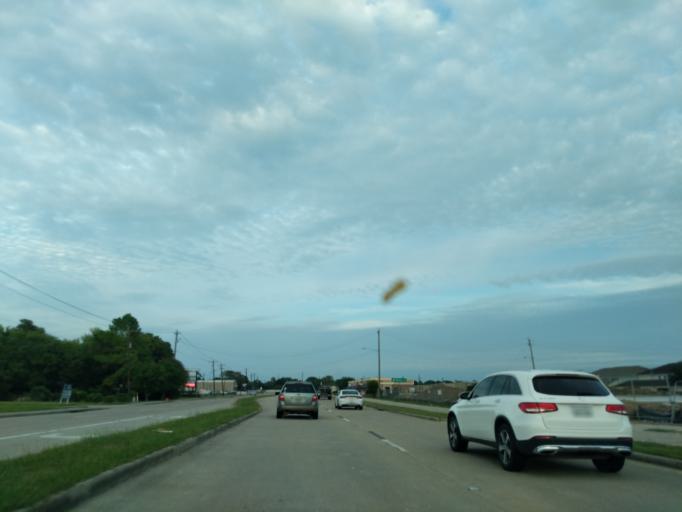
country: US
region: Texas
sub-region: Galveston County
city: Kemah
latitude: 29.5302
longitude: -95.0314
